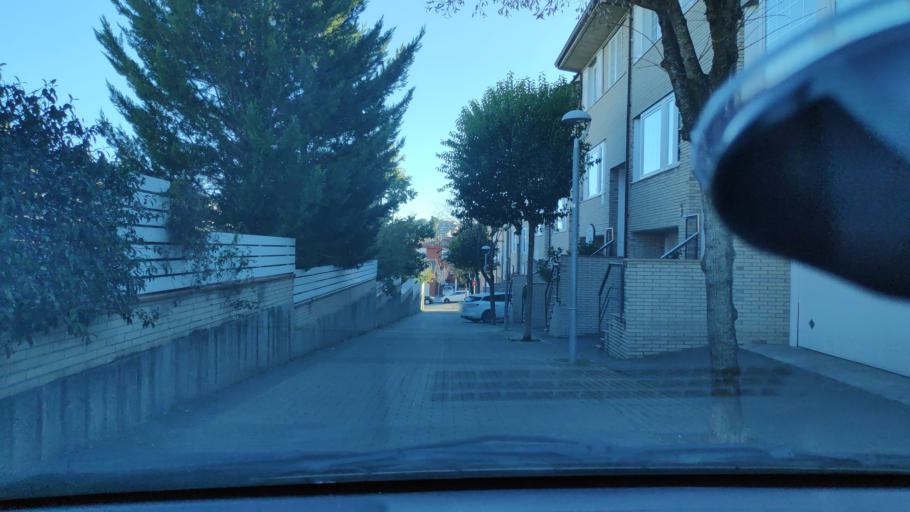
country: ES
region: Catalonia
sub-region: Provincia de Barcelona
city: Sant Quirze del Valles
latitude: 41.5285
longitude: 2.0688
